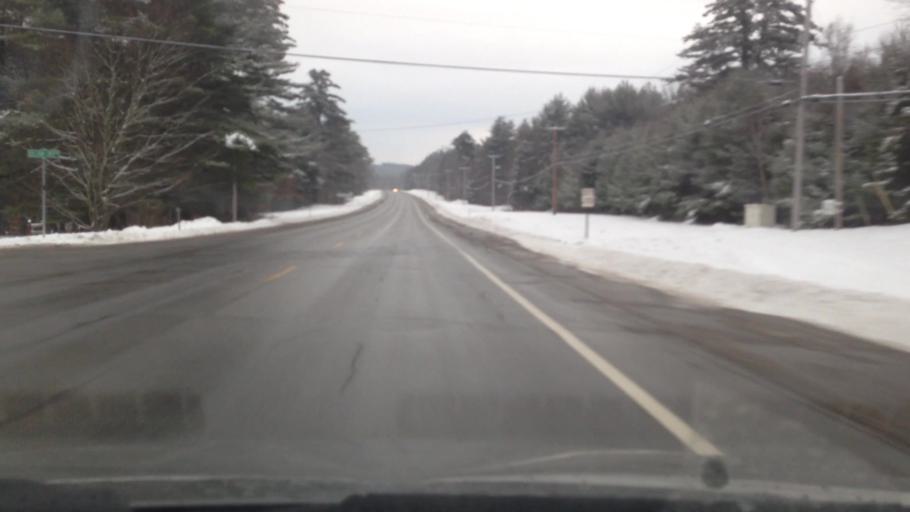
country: US
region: New Hampshire
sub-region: Cheshire County
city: Keene
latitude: 42.9894
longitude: -72.2582
